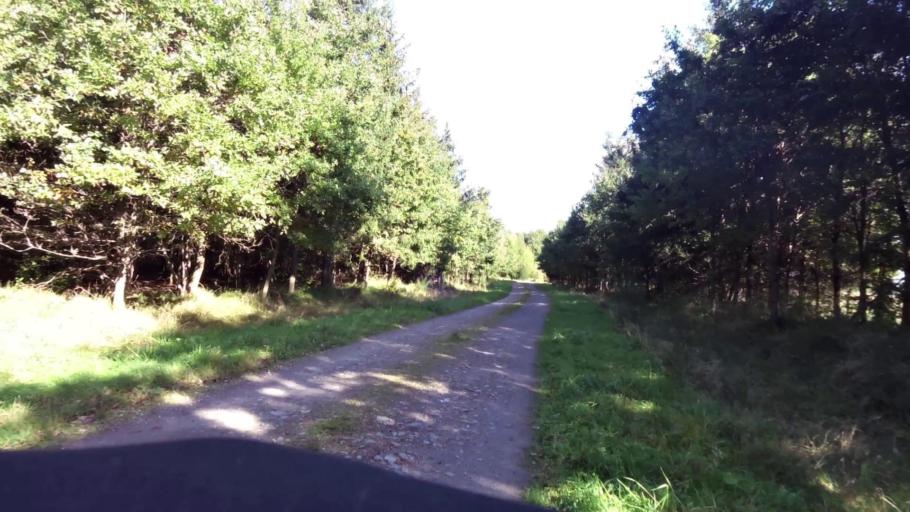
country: PL
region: West Pomeranian Voivodeship
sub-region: Powiat bialogardzki
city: Bialogard
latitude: 53.9961
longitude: 16.1214
